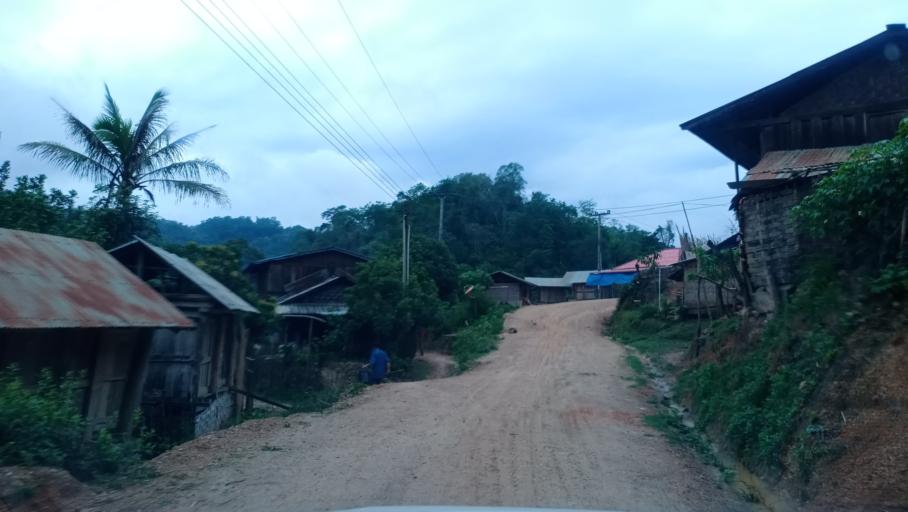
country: LA
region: Phongsali
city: Khoa
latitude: 21.2598
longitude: 102.6964
